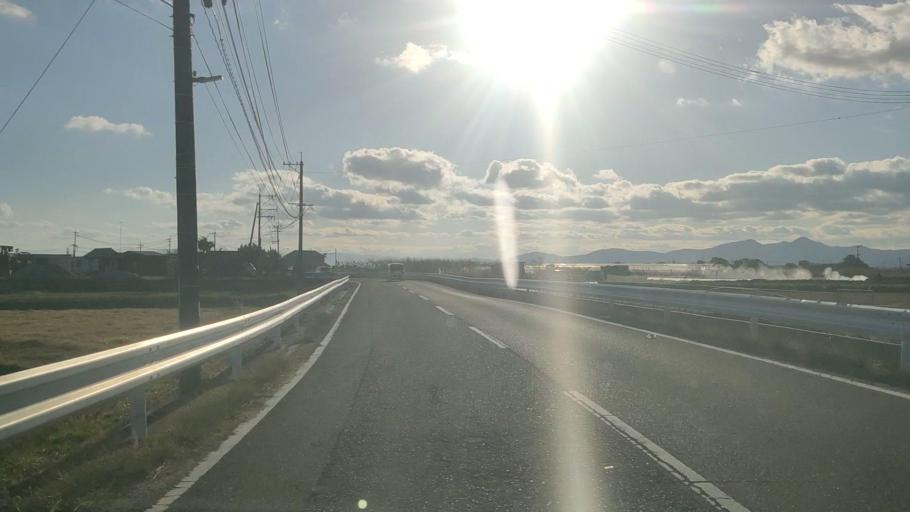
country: JP
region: Saga Prefecture
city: Saga-shi
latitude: 33.3012
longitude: 130.2517
